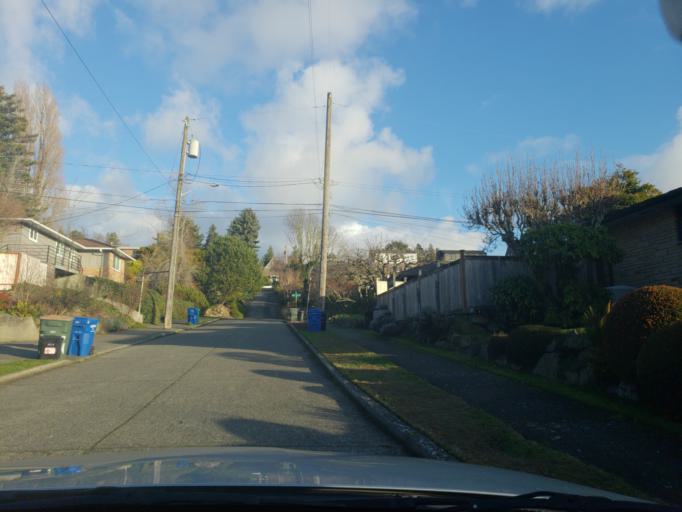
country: US
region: Washington
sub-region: King County
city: Seattle
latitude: 47.6377
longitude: -122.3977
